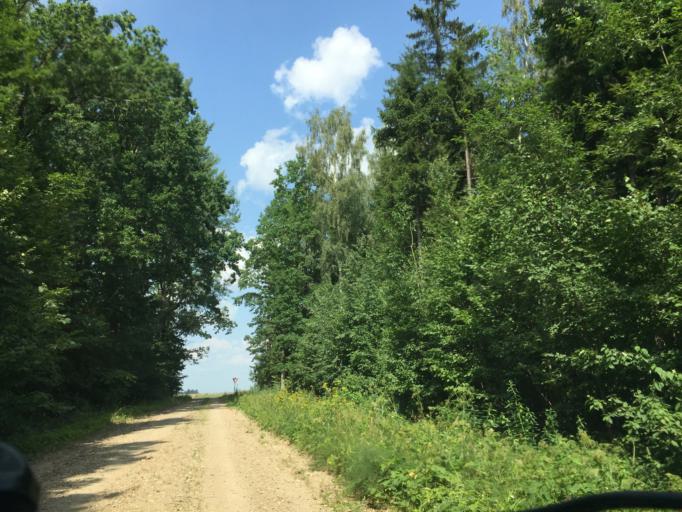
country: LT
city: Zagare
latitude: 56.3928
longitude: 23.2048
